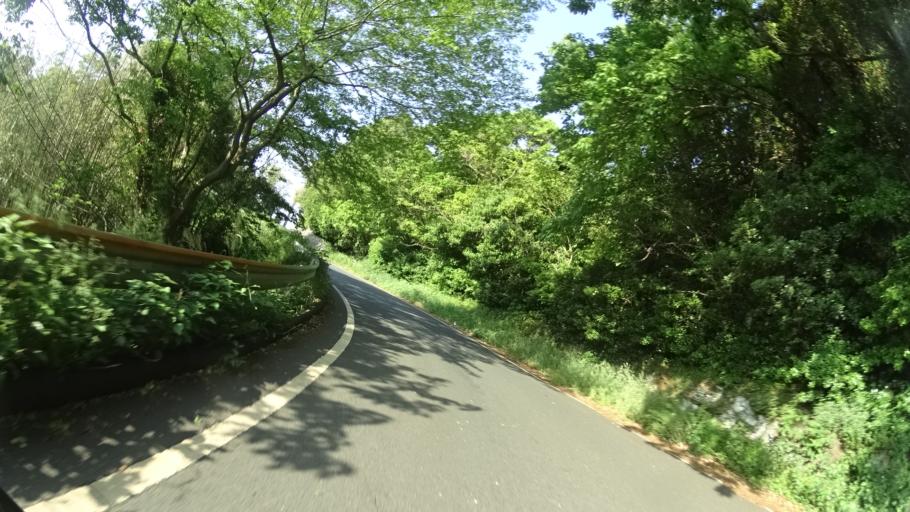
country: JP
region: Ehime
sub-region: Nishiuwa-gun
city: Ikata-cho
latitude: 33.3887
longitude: 132.0926
